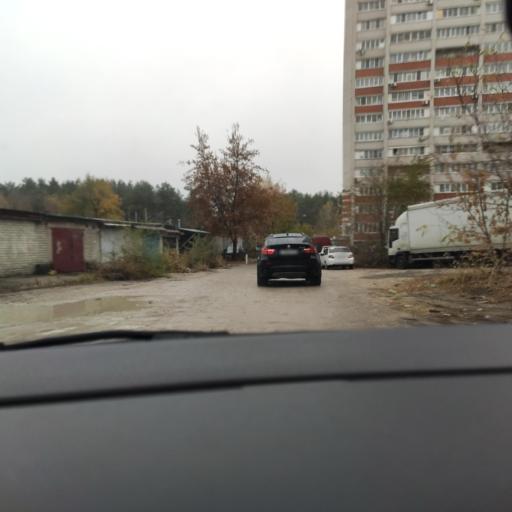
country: RU
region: Voronezj
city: Podgornoye
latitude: 51.6851
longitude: 39.1334
